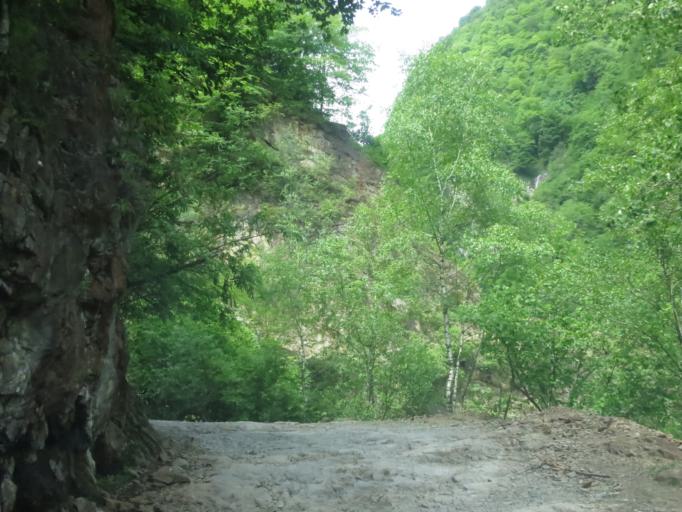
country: GE
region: Kakheti
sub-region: Telavi
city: Telavi
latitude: 42.2186
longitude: 45.4775
